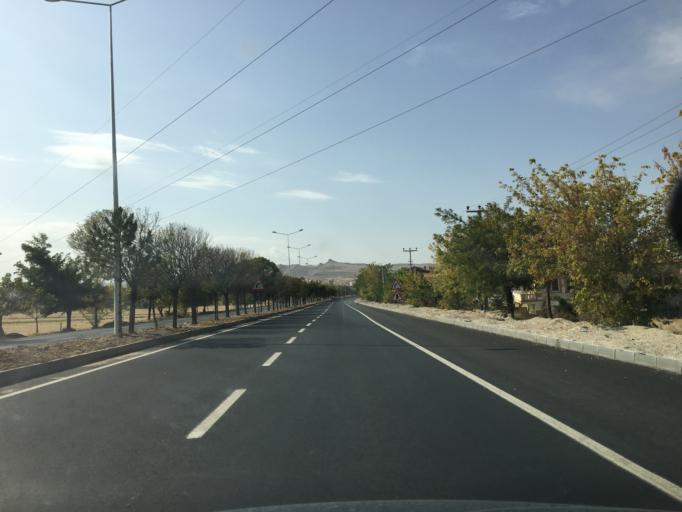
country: TR
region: Nevsehir
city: Avanos
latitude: 38.7042
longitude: 34.8511
